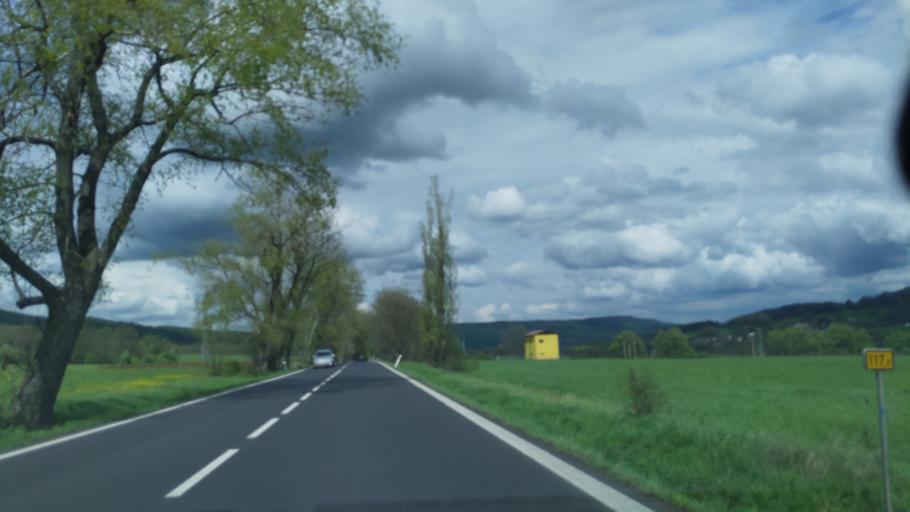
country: CZ
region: Ustecky
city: Libouchec
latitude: 50.7321
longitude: 14.0104
